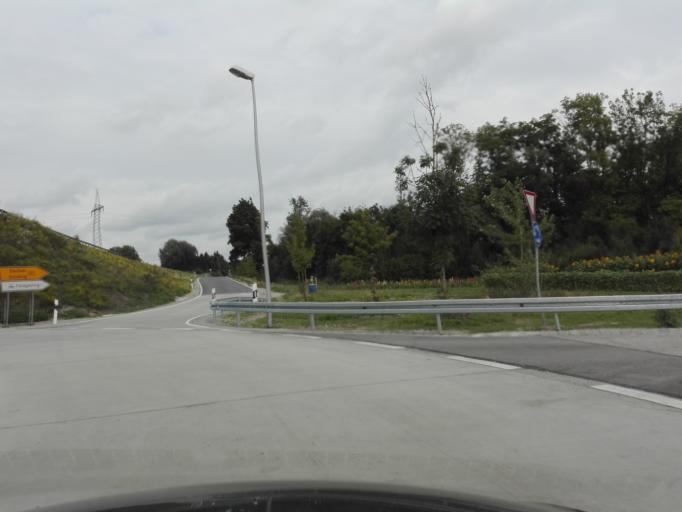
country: DE
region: Bavaria
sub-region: Upper Bavaria
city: Bergkirchen
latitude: 48.2365
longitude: 11.3542
